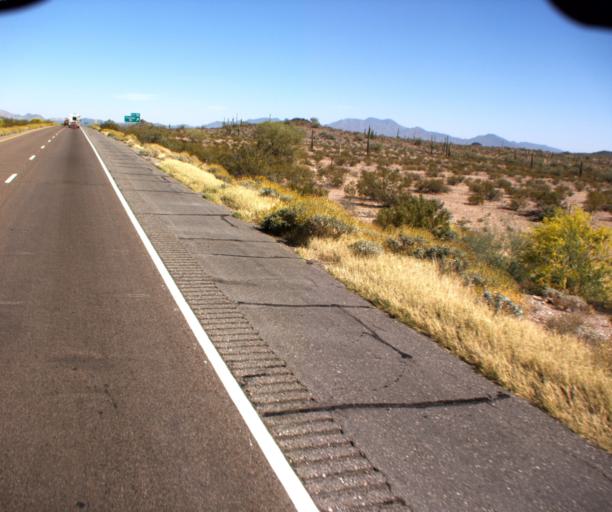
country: US
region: Arizona
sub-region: Pinal County
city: Maricopa
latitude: 32.8491
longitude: -112.3264
